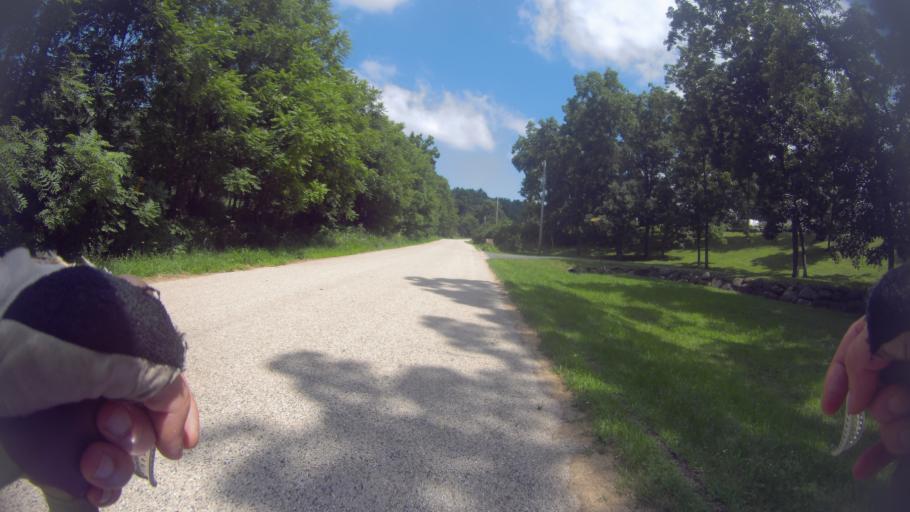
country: US
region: Wisconsin
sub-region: Sauk County
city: Sauk City
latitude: 43.2258
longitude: -89.6203
